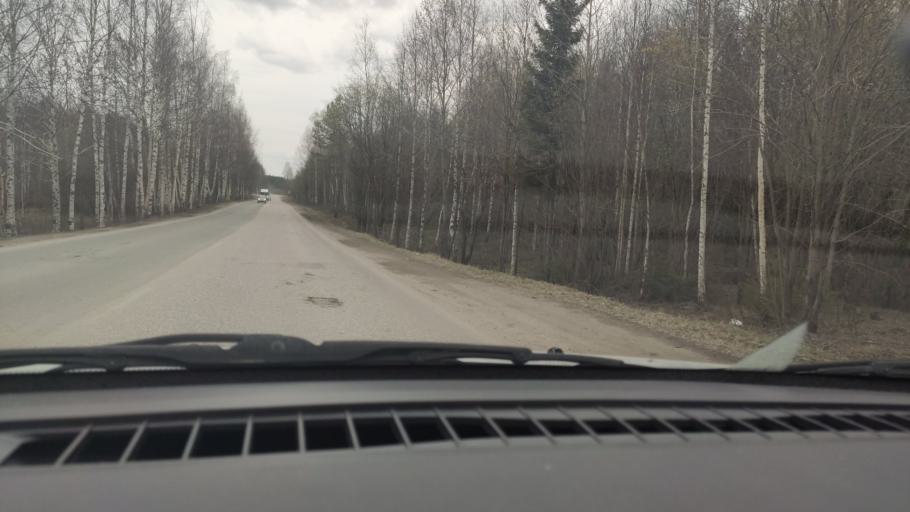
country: RU
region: Perm
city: Polazna
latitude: 58.1039
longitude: 56.4152
